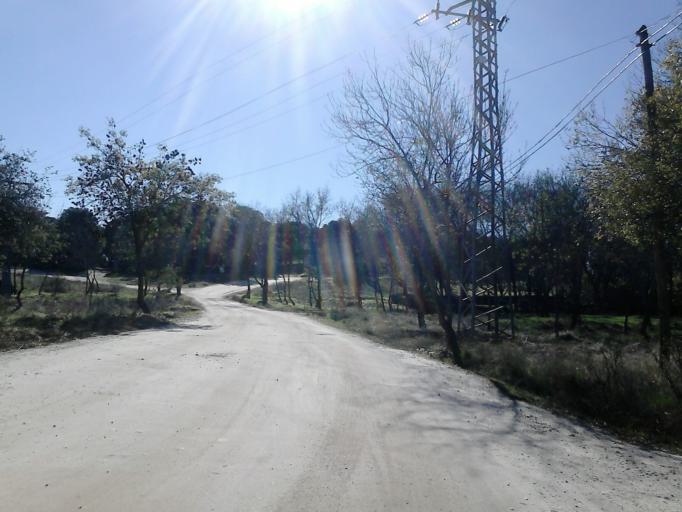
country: ES
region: Madrid
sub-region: Provincia de Madrid
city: Galapagar
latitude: 40.5650
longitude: -3.9776
